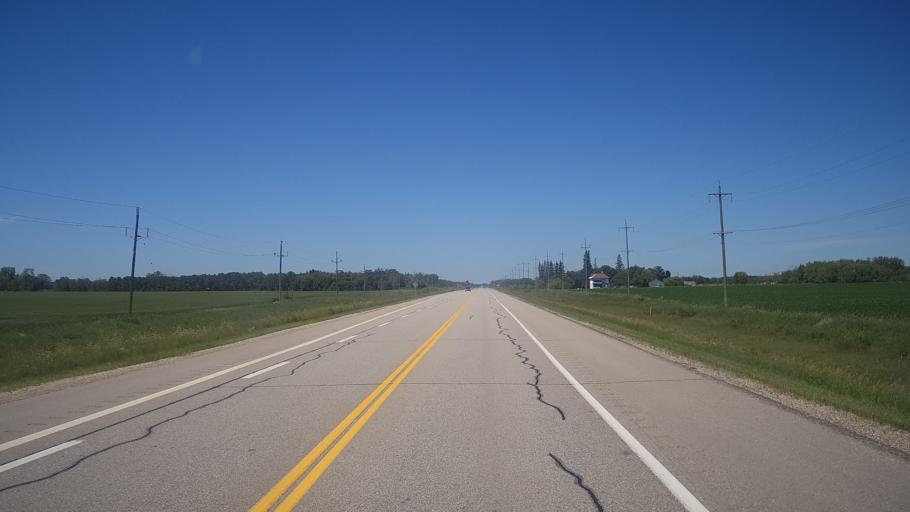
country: CA
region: Manitoba
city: Neepawa
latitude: 50.2253
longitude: -99.3314
